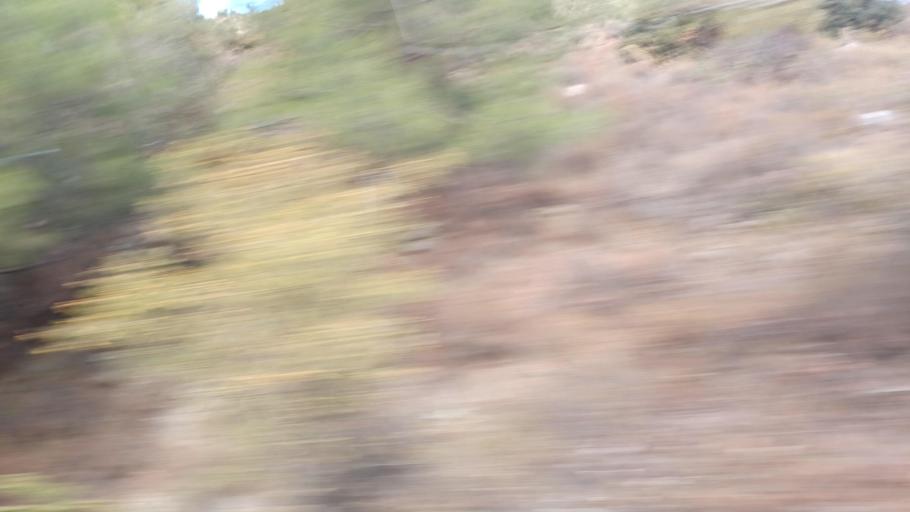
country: CY
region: Lefkosia
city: Kakopetria
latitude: 34.9784
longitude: 32.9090
